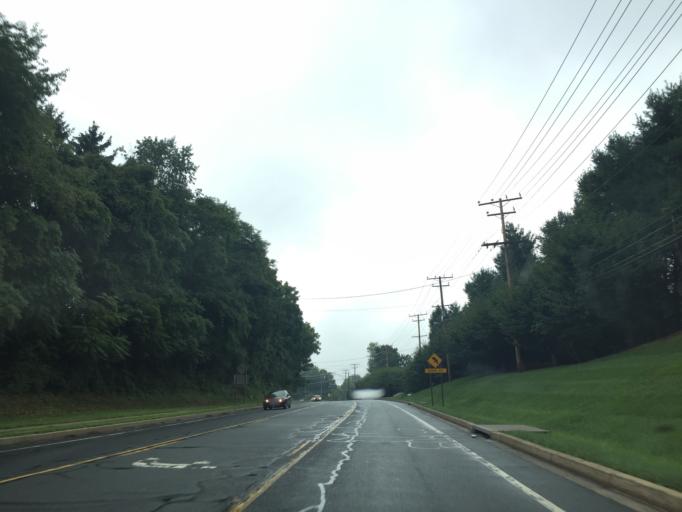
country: US
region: Maryland
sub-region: Harford County
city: Bel Air South
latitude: 39.5091
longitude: -76.3281
